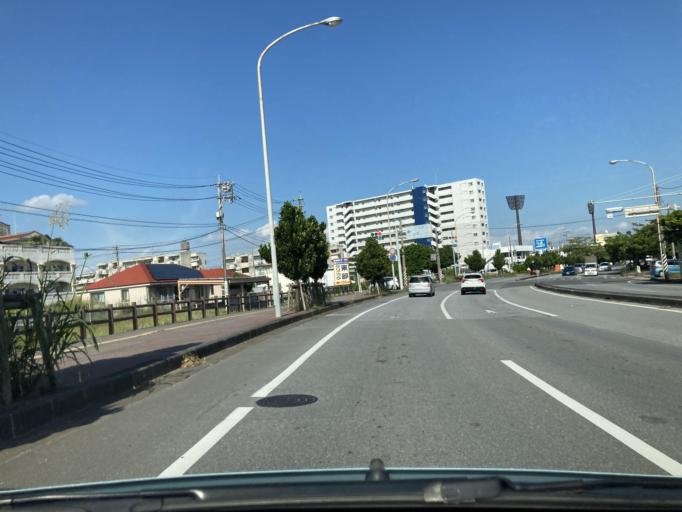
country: JP
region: Okinawa
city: Okinawa
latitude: 26.3060
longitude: 127.8165
